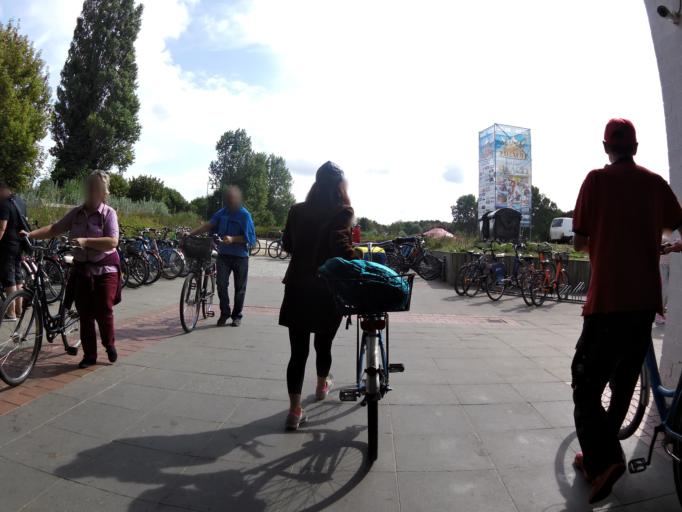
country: DE
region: Mecklenburg-Vorpommern
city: Seebad Heringsdorf
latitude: 53.9559
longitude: 14.1701
